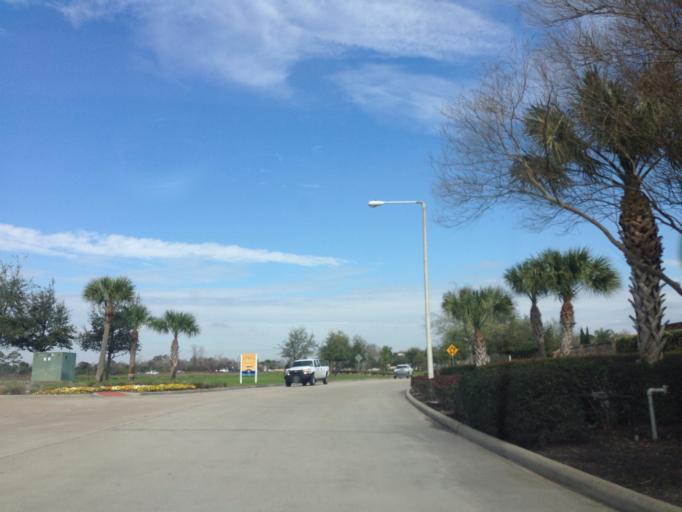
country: US
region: Texas
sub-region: Galveston County
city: Kemah
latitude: 29.5156
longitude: -95.0225
